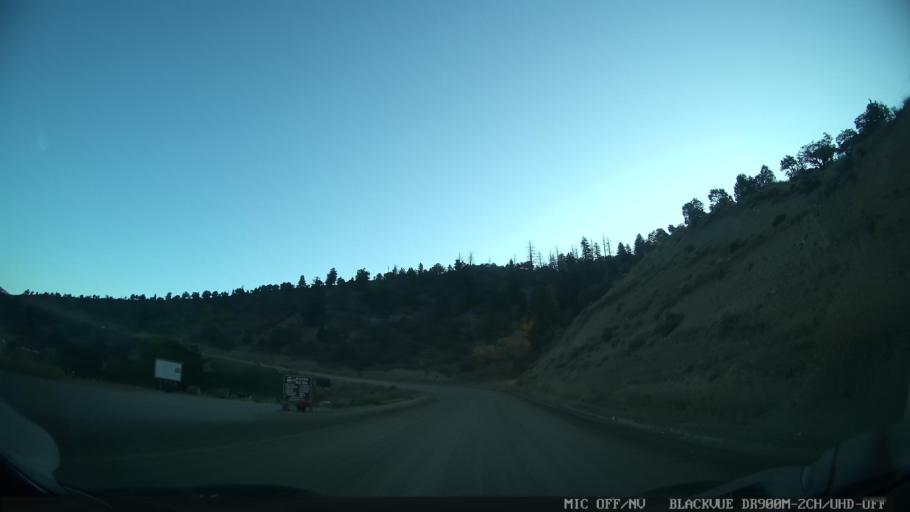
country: US
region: Colorado
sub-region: Eagle County
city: Edwards
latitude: 39.8935
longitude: -106.6080
